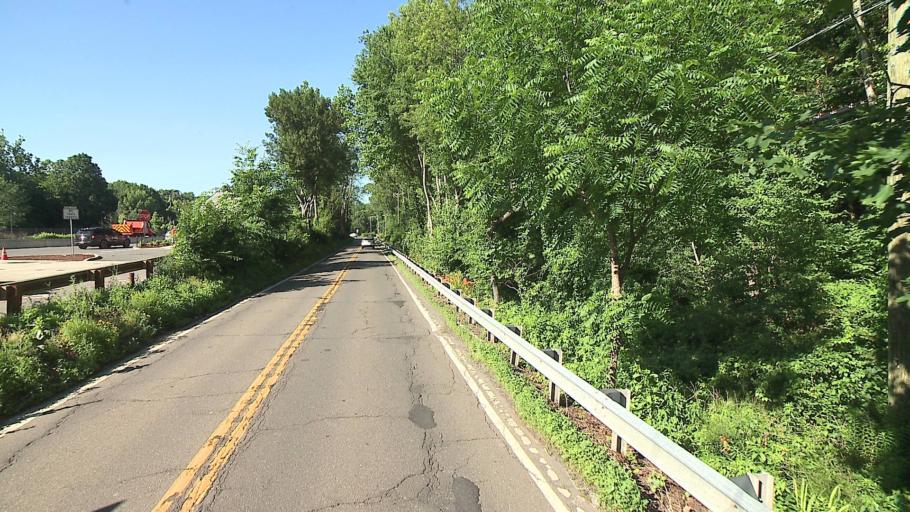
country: US
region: Connecticut
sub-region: Fairfield County
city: Trumbull
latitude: 41.2194
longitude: -73.2563
